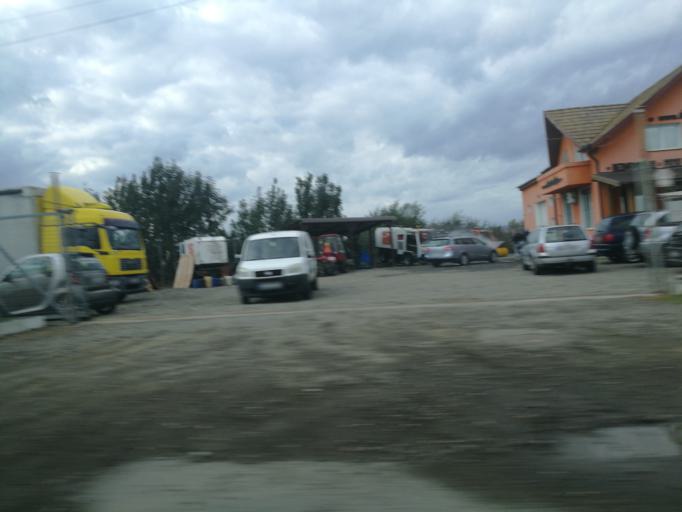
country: RO
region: Mures
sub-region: Comuna Cristesti
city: Cristesti
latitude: 46.4979
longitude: 24.4829
